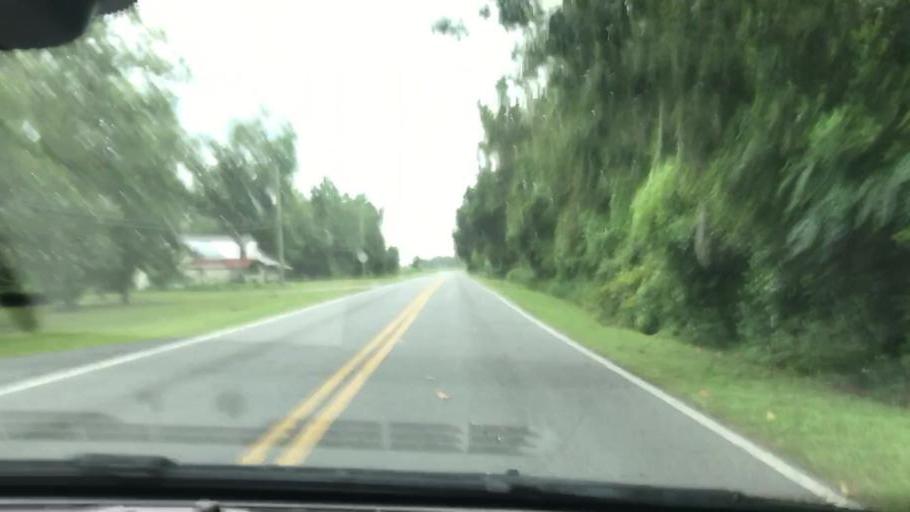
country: US
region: Florida
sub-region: Madison County
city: Madison
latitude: 30.4162
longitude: -83.3004
